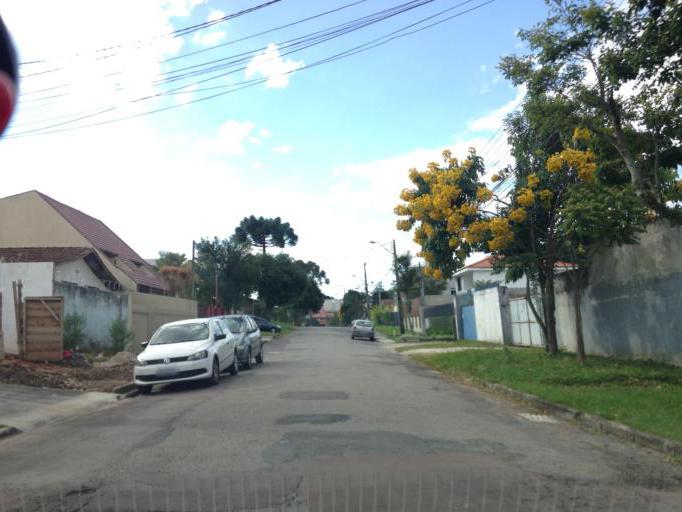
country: BR
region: Parana
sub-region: Pinhais
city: Pinhais
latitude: -25.4154
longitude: -49.2242
